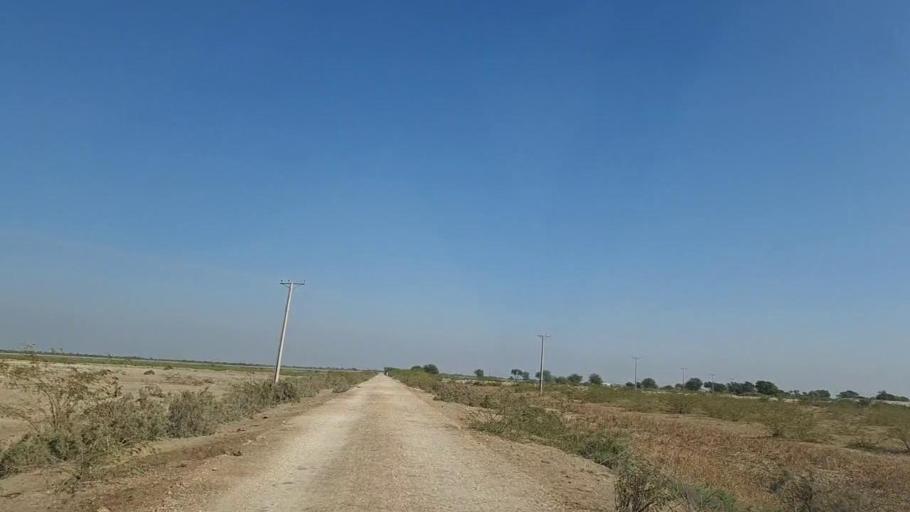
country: PK
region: Sindh
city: Samaro
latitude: 25.3990
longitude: 69.4258
